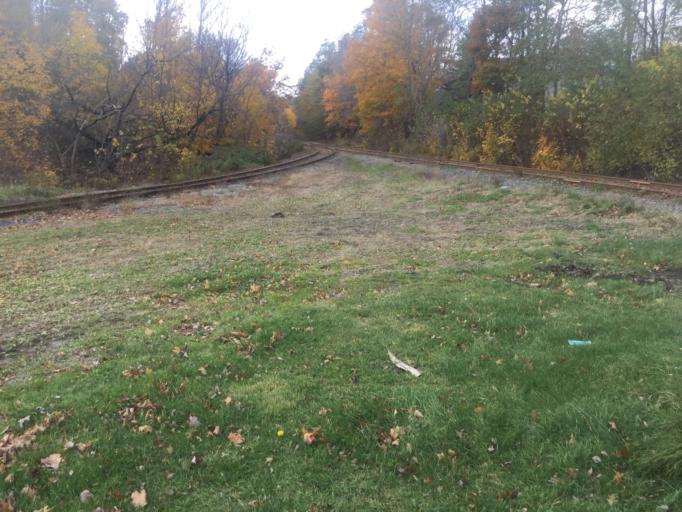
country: CA
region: Nova Scotia
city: New Glasgow
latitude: 45.5549
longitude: -62.6613
